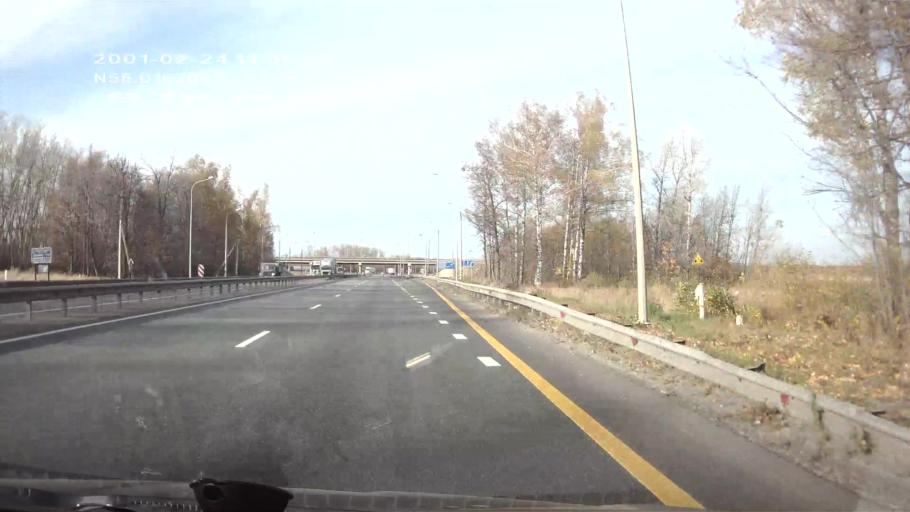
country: RU
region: Chuvashia
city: Kugesi
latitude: 56.0159
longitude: 47.3089
